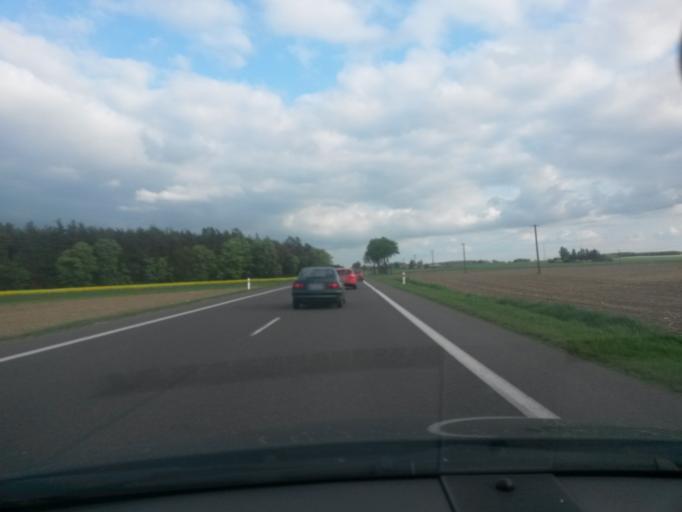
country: PL
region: Masovian Voivodeship
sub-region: Powiat plocki
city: Starozreby
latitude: 52.6622
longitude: 20.0772
